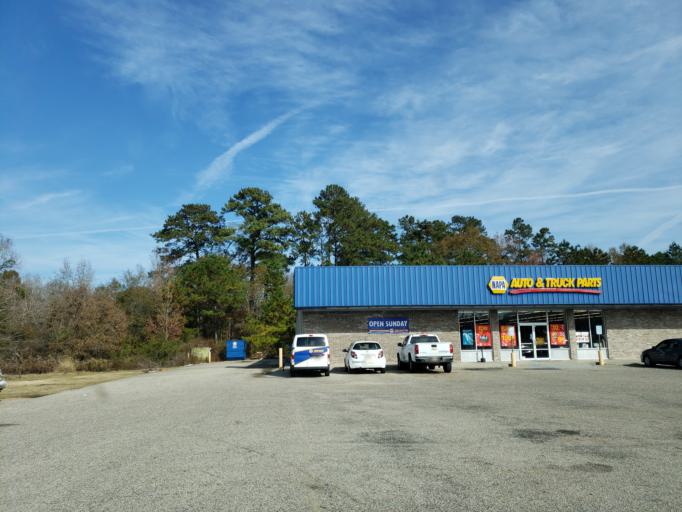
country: US
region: Mississippi
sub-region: Forrest County
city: Rawls Springs
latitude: 31.3795
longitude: -89.3655
